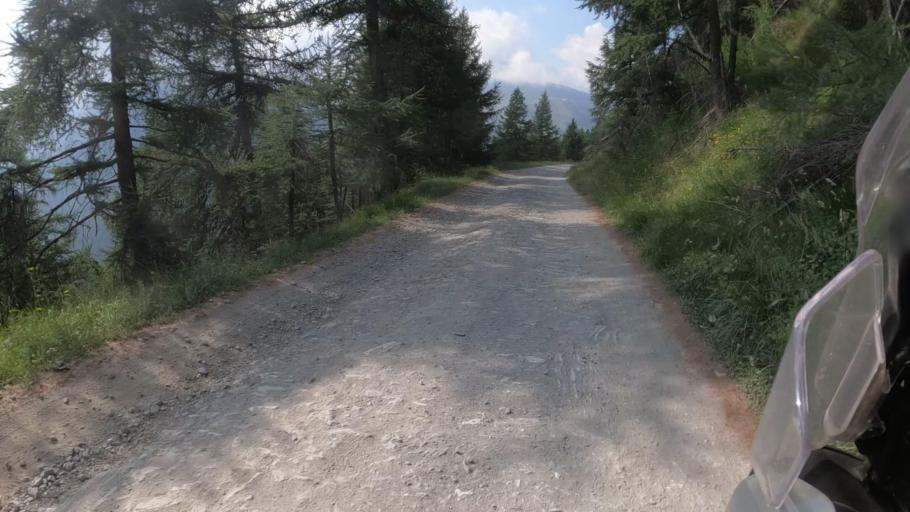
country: IT
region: Piedmont
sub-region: Provincia di Torino
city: Sestriere
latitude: 44.9739
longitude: 6.8822
